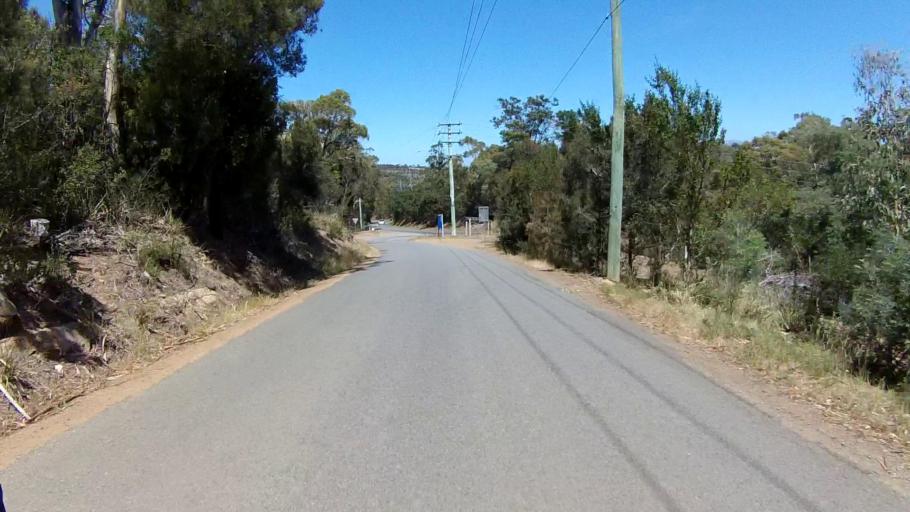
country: AU
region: Tasmania
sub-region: Clarence
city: Howrah
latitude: -42.8553
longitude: 147.4211
